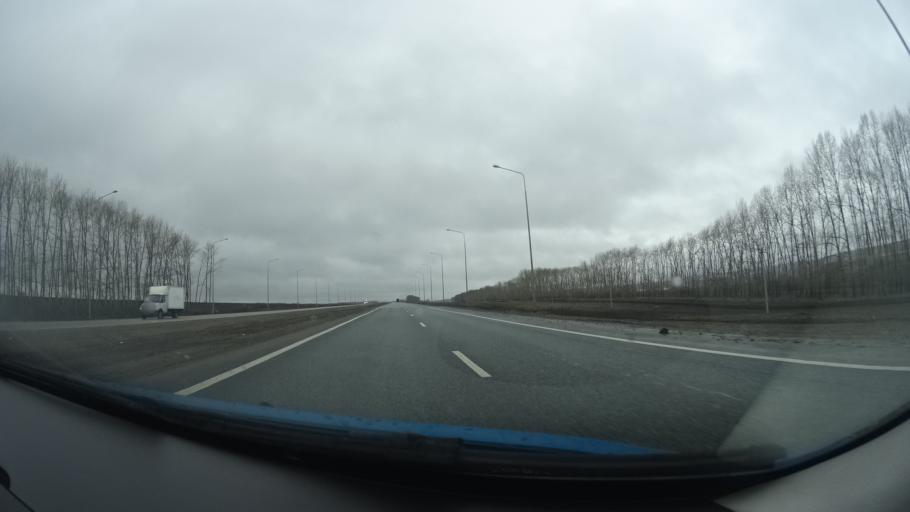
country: RU
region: Bashkortostan
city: Alekseyevka
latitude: 54.7274
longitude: 54.9493
